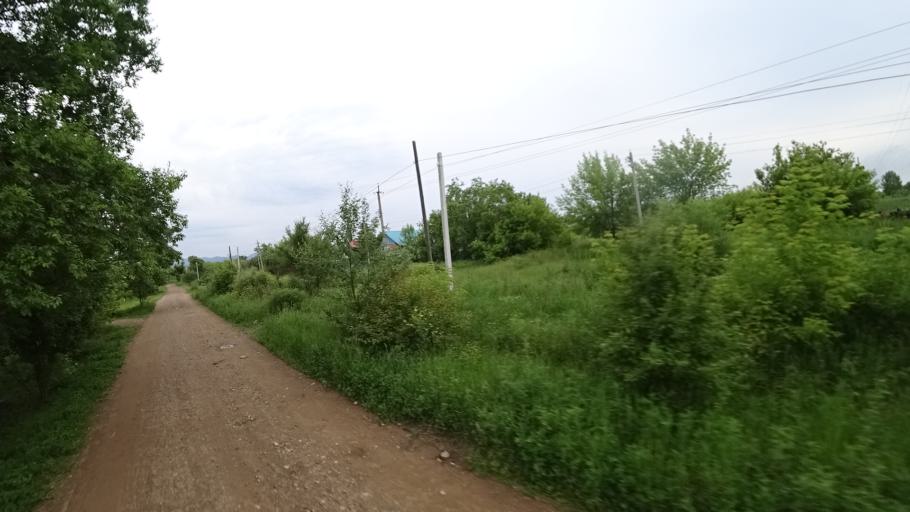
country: RU
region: Primorskiy
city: Novosysoyevka
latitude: 44.2321
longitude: 133.3656
